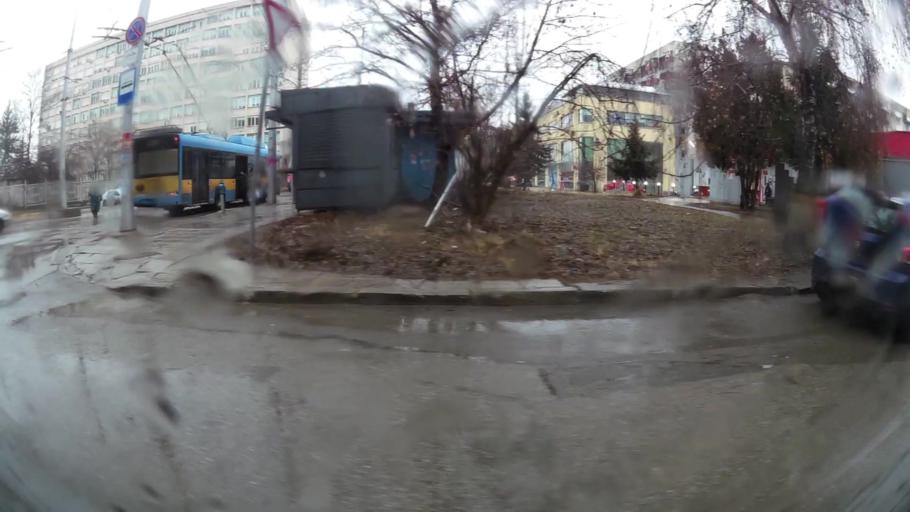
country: BG
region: Sofia-Capital
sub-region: Stolichna Obshtina
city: Sofia
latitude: 42.6601
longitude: 23.3744
